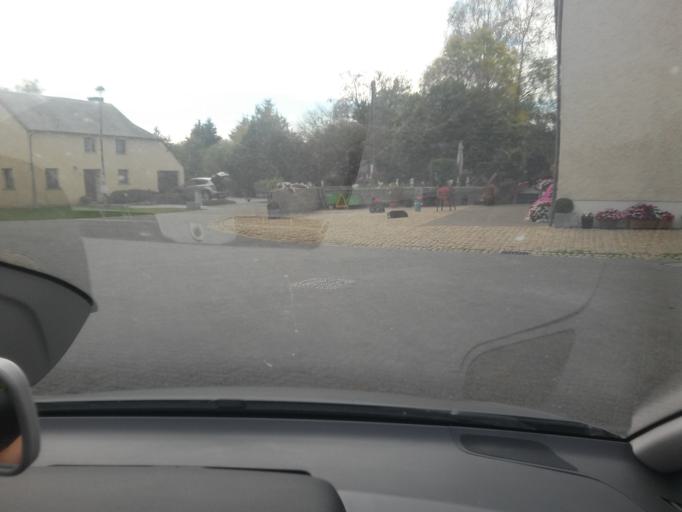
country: BE
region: Wallonia
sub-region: Province du Luxembourg
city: Attert
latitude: 49.7087
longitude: 5.7258
